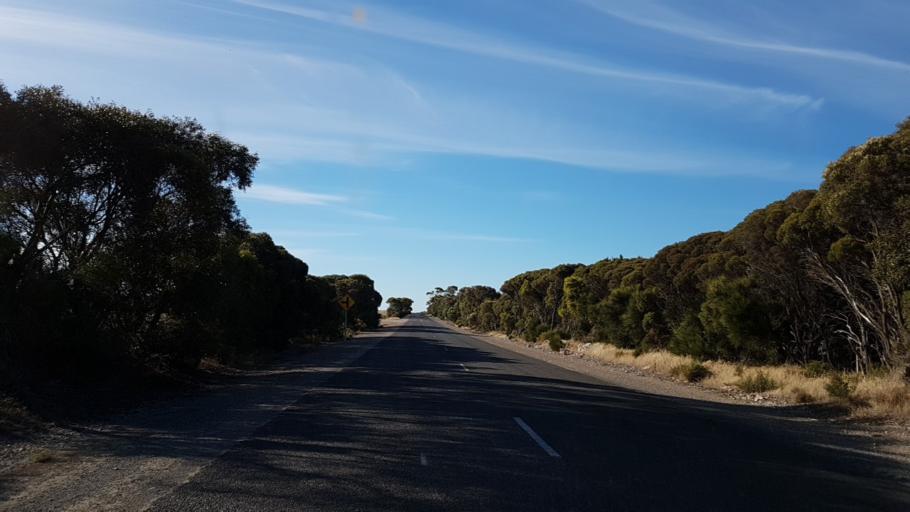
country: AU
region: South Australia
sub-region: Yorke Peninsula
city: Honiton
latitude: -34.9531
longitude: 137.1005
